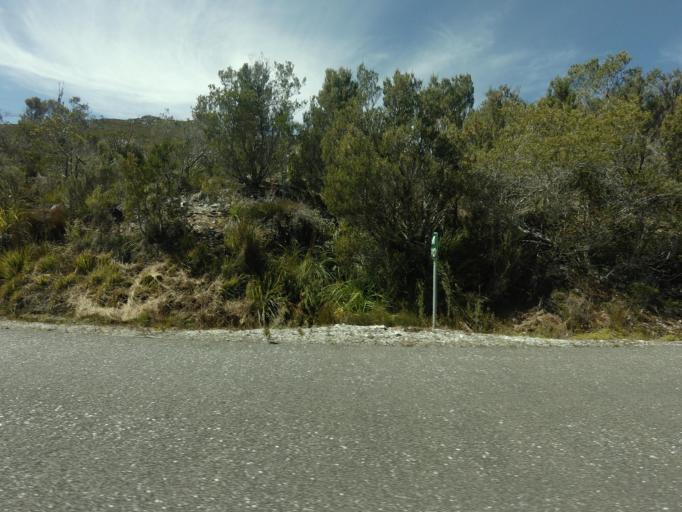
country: AU
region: Tasmania
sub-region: West Coast
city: Queenstown
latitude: -42.7719
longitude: 146.0573
